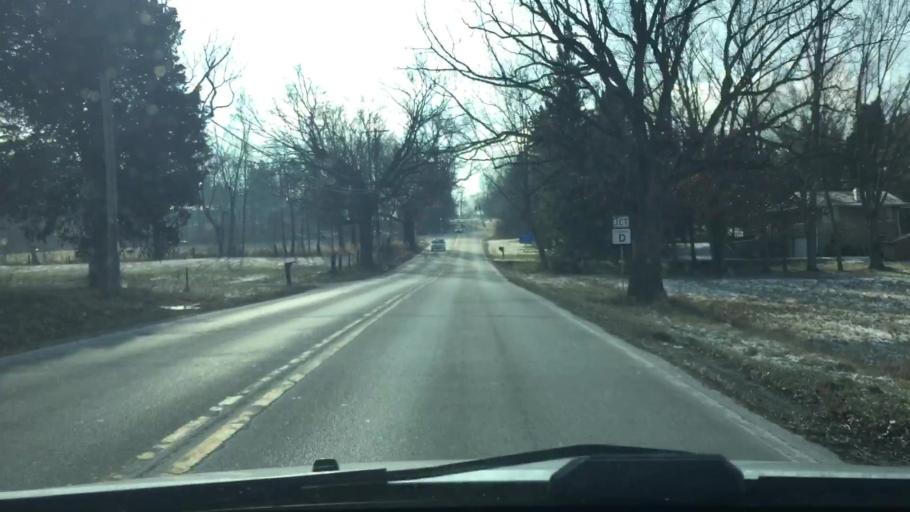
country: US
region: Wisconsin
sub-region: Waukesha County
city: Waukesha
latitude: 42.9902
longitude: -88.2891
